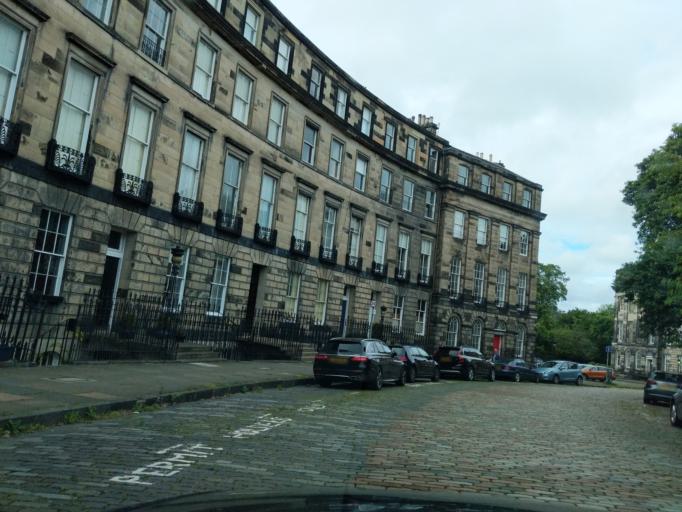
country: GB
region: Scotland
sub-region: Edinburgh
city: Edinburgh
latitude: 55.9535
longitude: -3.2106
